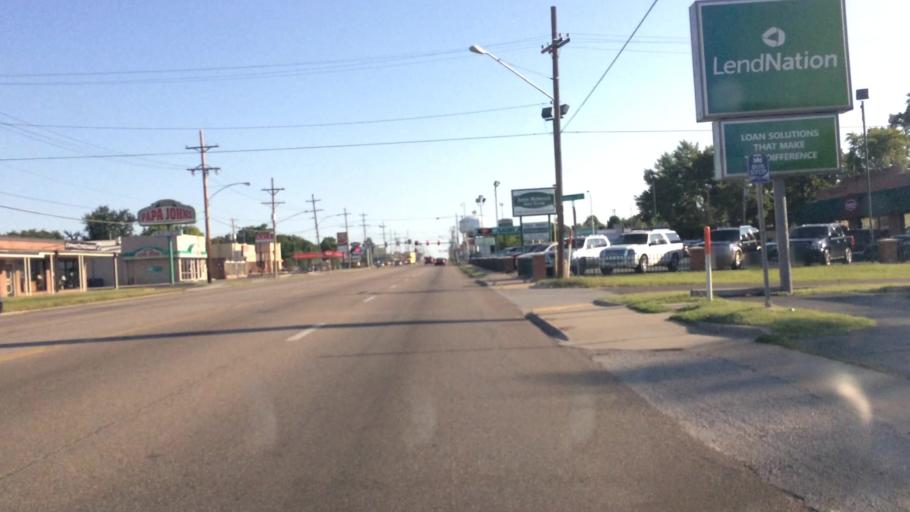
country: US
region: Missouri
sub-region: Greene County
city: Springfield
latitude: 37.1943
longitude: -93.2621
